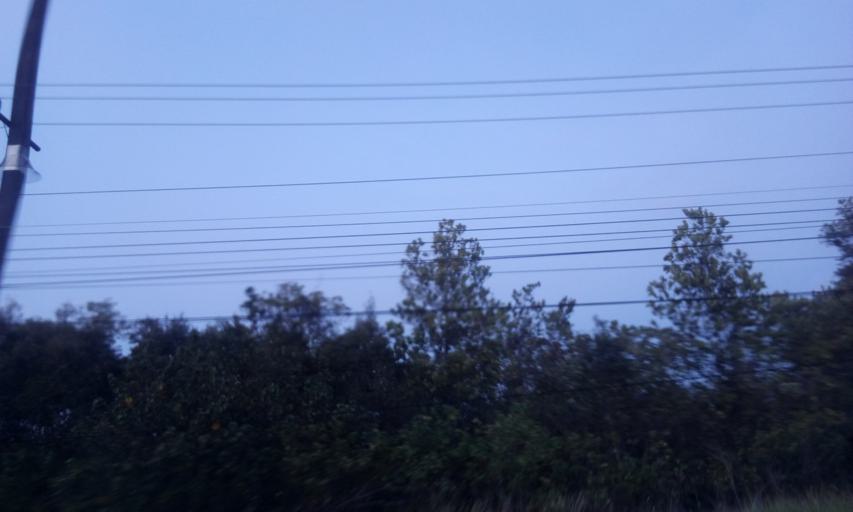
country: TH
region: Trat
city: Khao Saming
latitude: 12.3903
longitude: 102.3679
